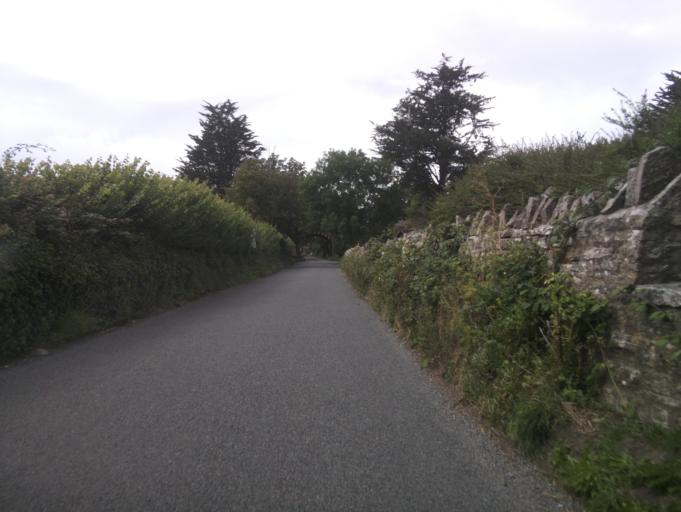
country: GB
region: England
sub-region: Somerset
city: Ilchester
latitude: 51.0562
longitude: -2.6697
